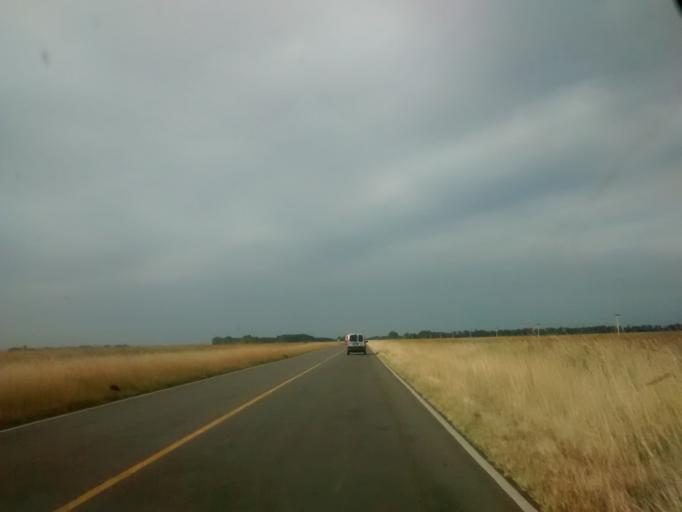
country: AR
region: Buenos Aires
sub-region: Partido de Ayacucho
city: Ayacucho
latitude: -36.6819
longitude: -58.5750
